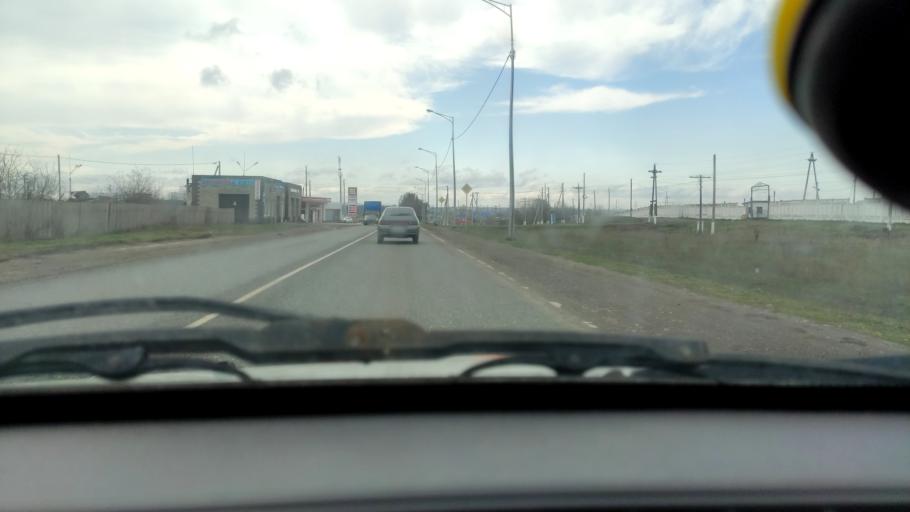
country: RU
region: Samara
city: Zhigulevsk
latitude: 53.5576
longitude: 49.5365
